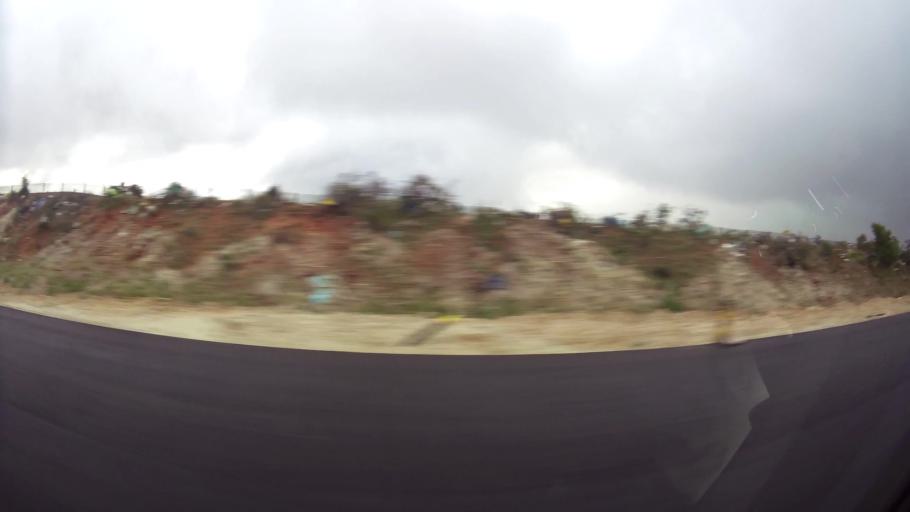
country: ZA
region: Eastern Cape
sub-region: Nelson Mandela Bay Metropolitan Municipality
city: Port Elizabeth
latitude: -33.8288
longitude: 25.5124
